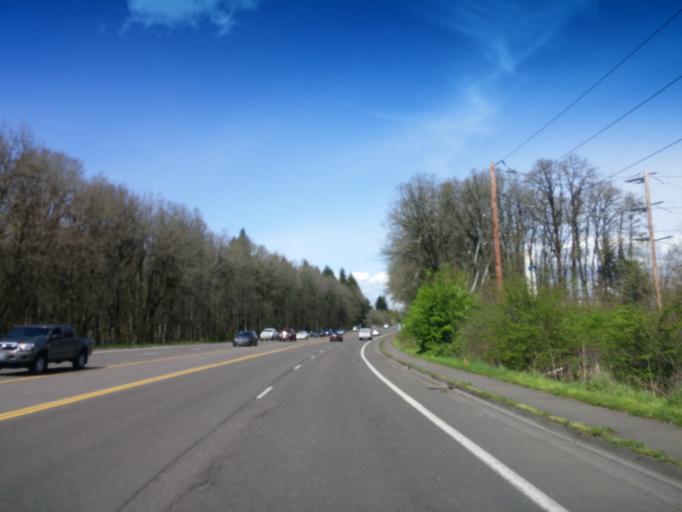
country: US
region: Oregon
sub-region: Washington County
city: Beaverton
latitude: 45.5006
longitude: -122.8283
